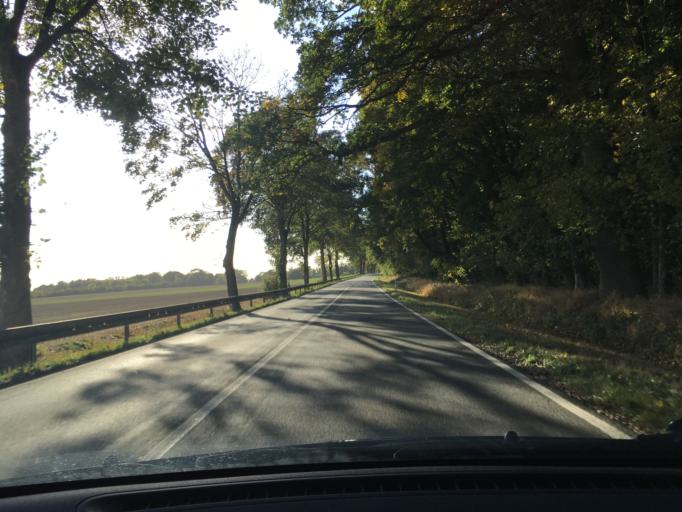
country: DE
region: Lower Saxony
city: Neu Darchau
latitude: 53.3845
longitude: 10.9040
